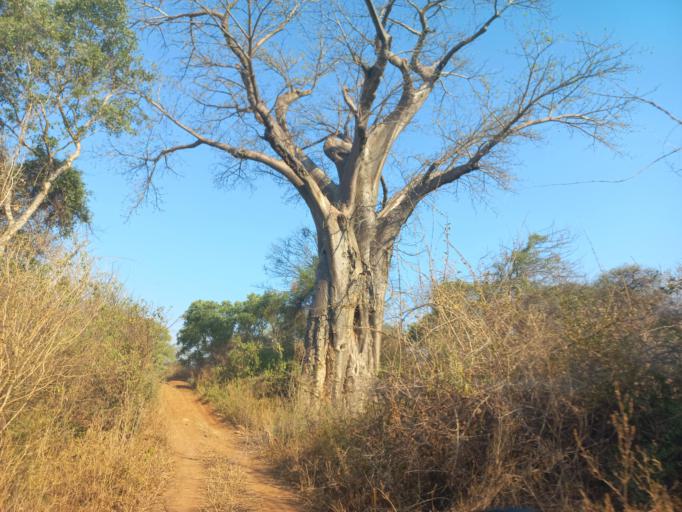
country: ZM
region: Lusaka
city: Luangwa
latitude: -15.4171
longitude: 30.2451
